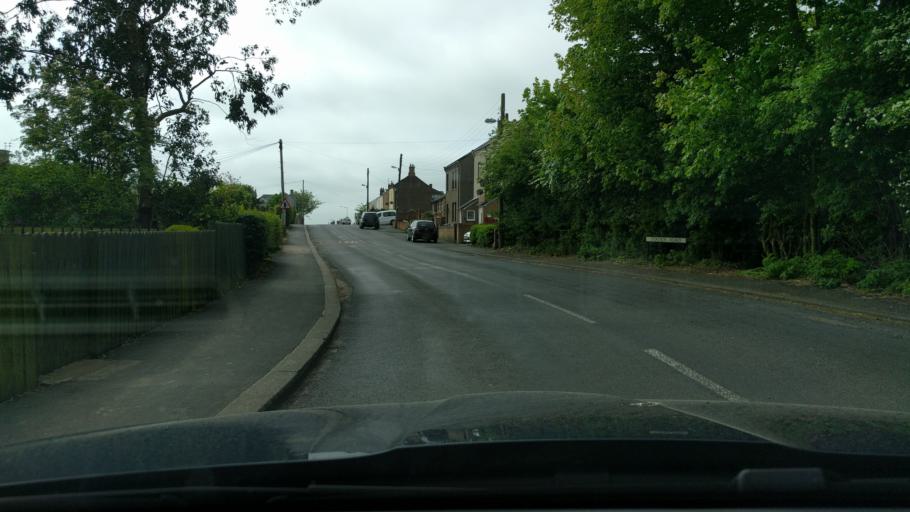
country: GB
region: England
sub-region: Northumberland
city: Acklington
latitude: 55.3060
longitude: -1.6148
